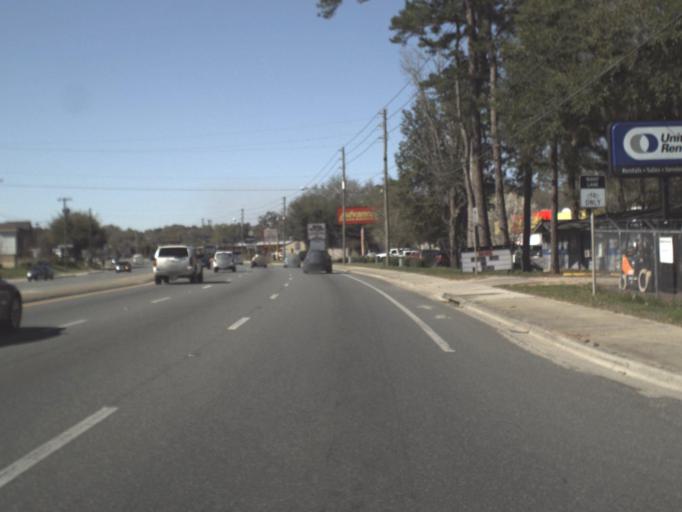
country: US
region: Florida
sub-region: Leon County
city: Tallahassee
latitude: 30.4850
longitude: -84.2370
